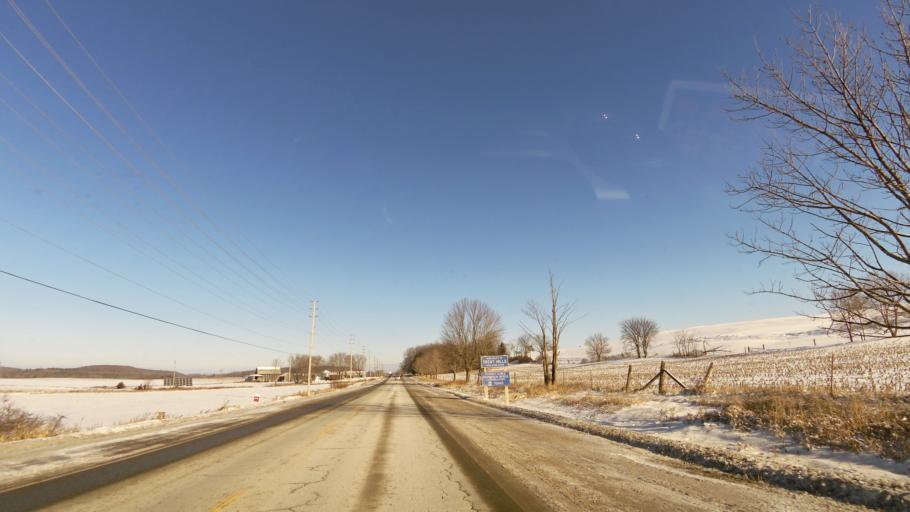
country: CA
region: Ontario
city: Quinte West
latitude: 44.2250
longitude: -77.8246
